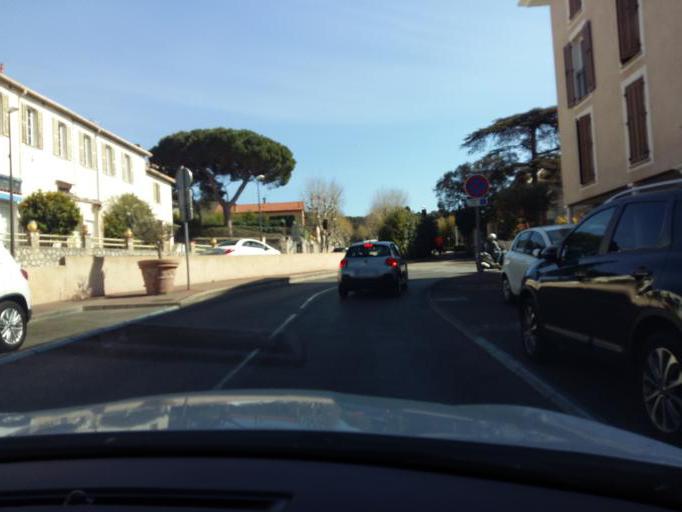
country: FR
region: Provence-Alpes-Cote d'Azur
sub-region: Departement du Var
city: Ollioules
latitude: 43.1369
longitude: 5.8506
